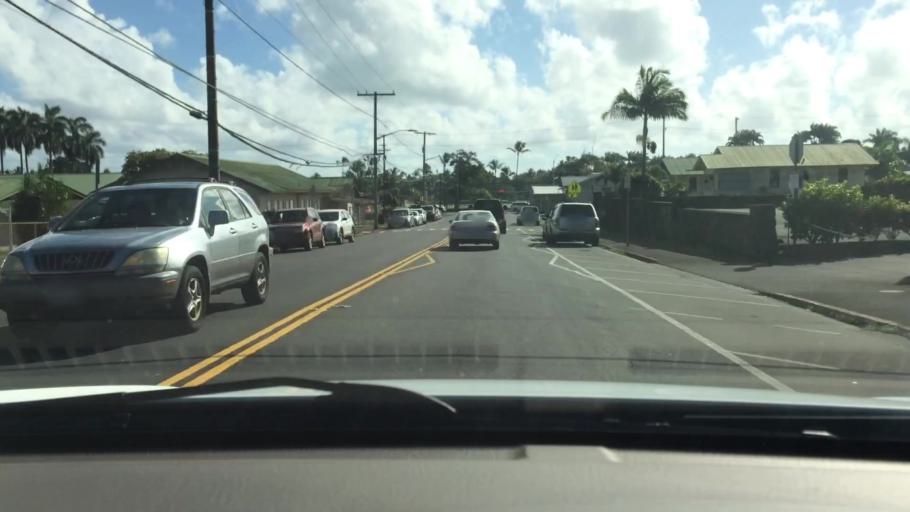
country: US
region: Hawaii
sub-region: Hawaii County
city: Hilo
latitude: 19.7127
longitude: -155.0788
